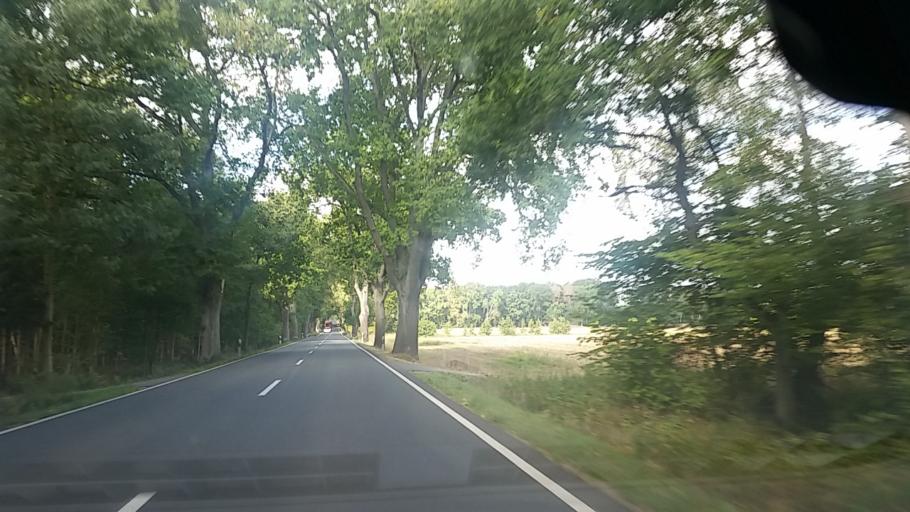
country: DE
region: Saxony-Anhalt
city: Jubar
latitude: 52.6806
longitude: 10.8332
